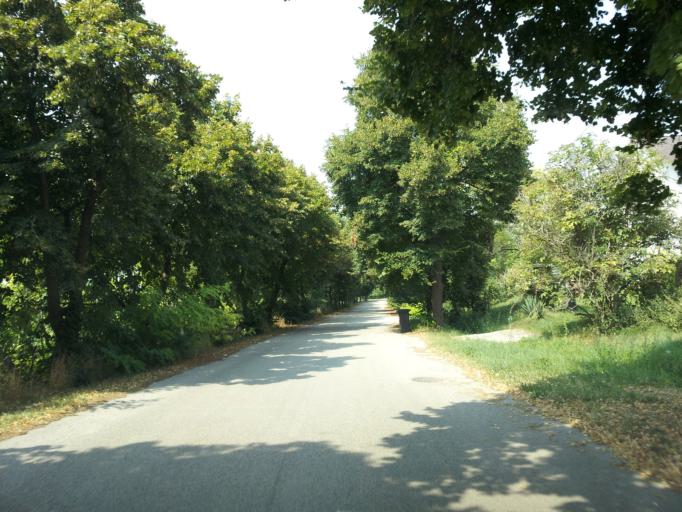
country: HU
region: Gyor-Moson-Sopron
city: Pannonhalma
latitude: 47.5053
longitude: 17.7884
